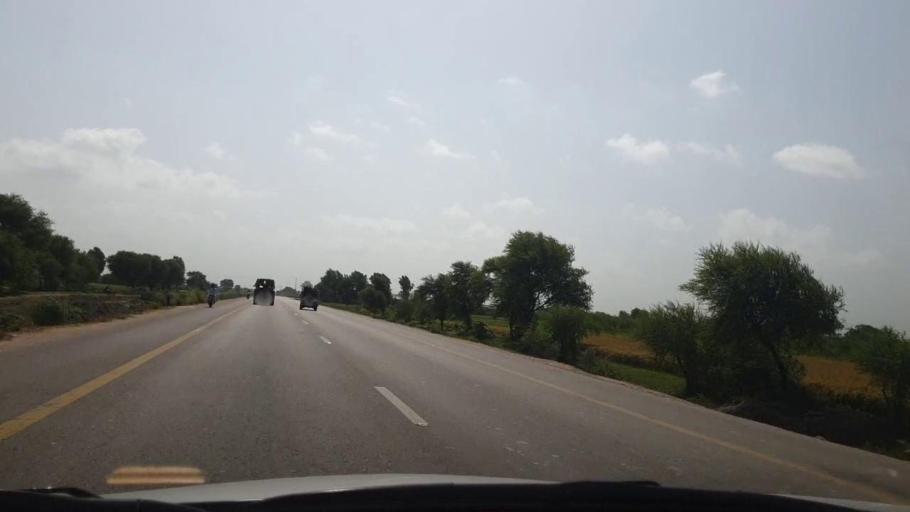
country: PK
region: Sindh
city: Matli
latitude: 24.9778
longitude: 68.6701
